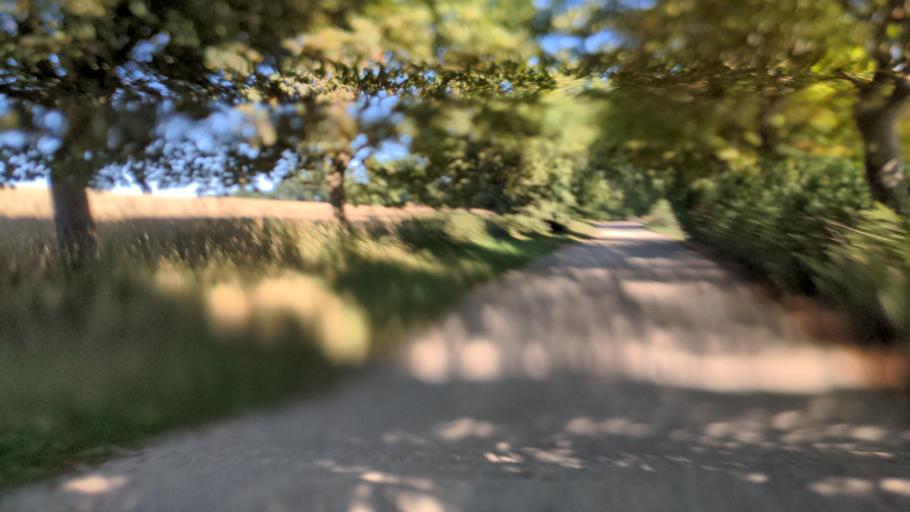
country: DE
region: Mecklenburg-Vorpommern
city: Klutz
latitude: 53.9784
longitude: 11.1706
